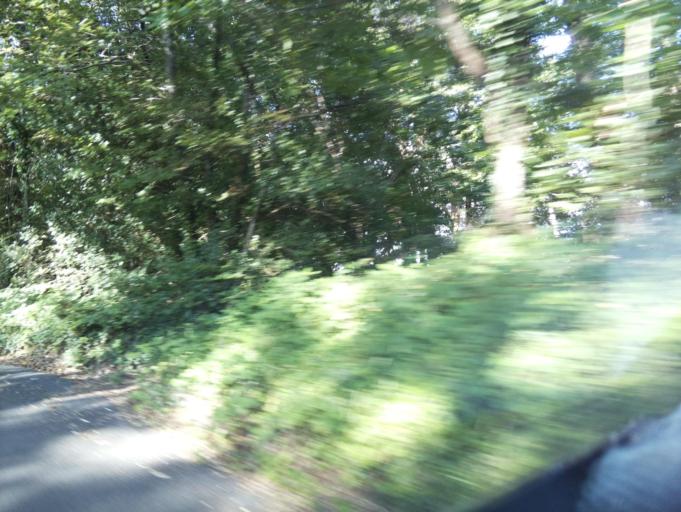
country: GB
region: England
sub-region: Devon
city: Buckfastleigh
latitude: 50.5218
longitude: -3.8059
